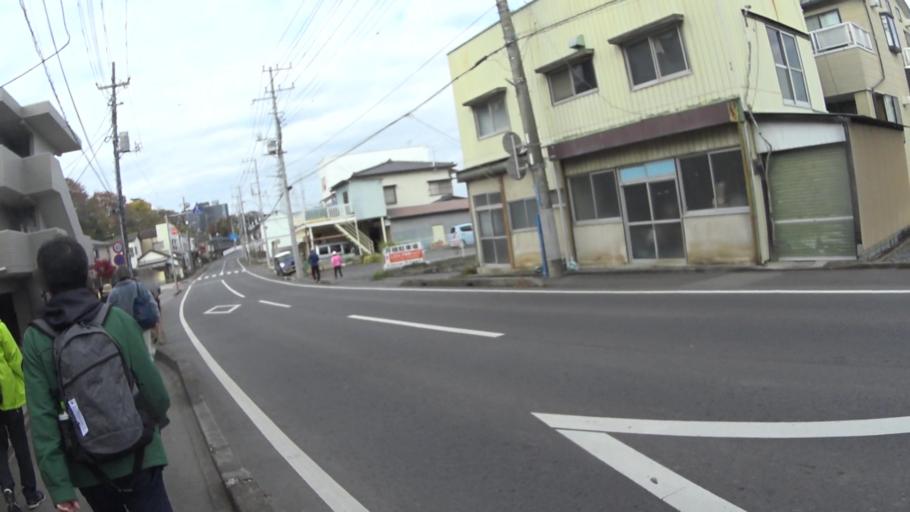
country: JP
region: Ibaraki
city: Mito-shi
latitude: 36.3753
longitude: 140.4828
